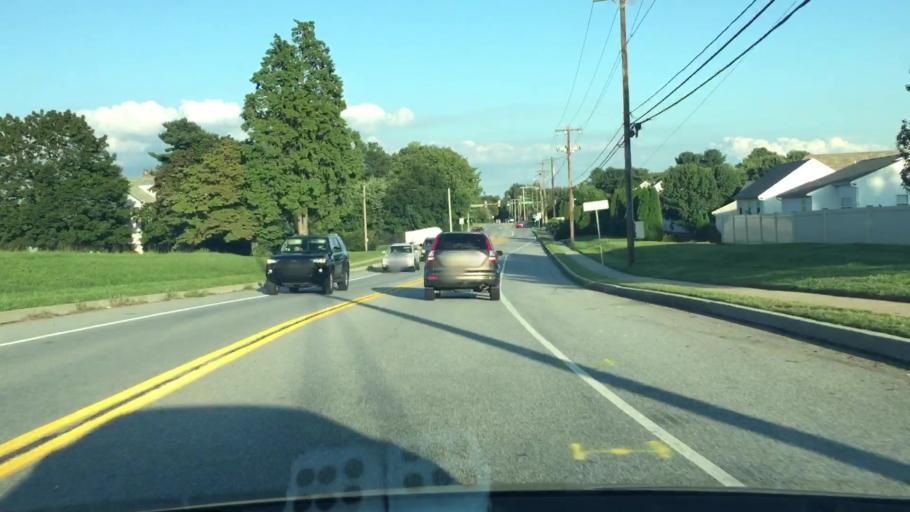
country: US
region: Pennsylvania
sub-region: Delaware County
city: Boothwyn
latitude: 39.8354
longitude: -75.4713
